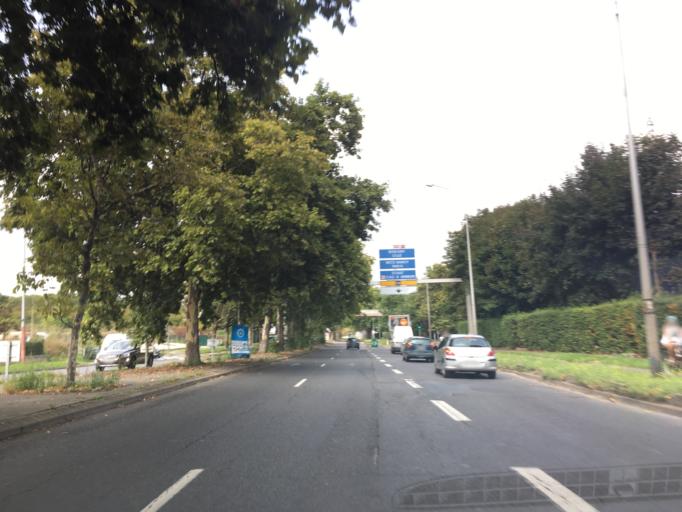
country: FR
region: Ile-de-France
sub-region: Departement du Val-de-Marne
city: Choisy-le-Roi
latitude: 48.7809
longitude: 2.4377
